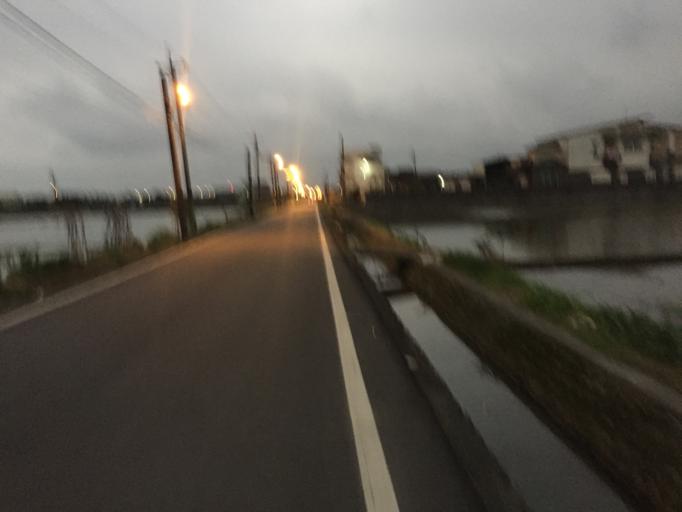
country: TW
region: Taiwan
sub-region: Yilan
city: Yilan
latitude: 24.6587
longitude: 121.7802
